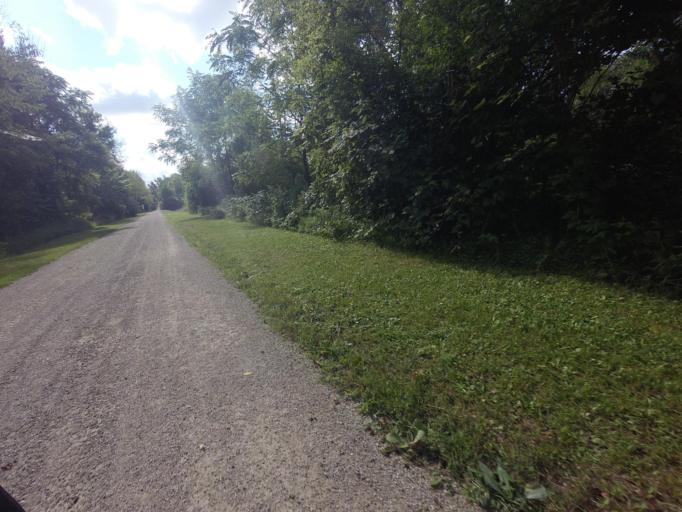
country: CA
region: Ontario
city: Huron East
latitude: 43.7362
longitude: -81.4227
